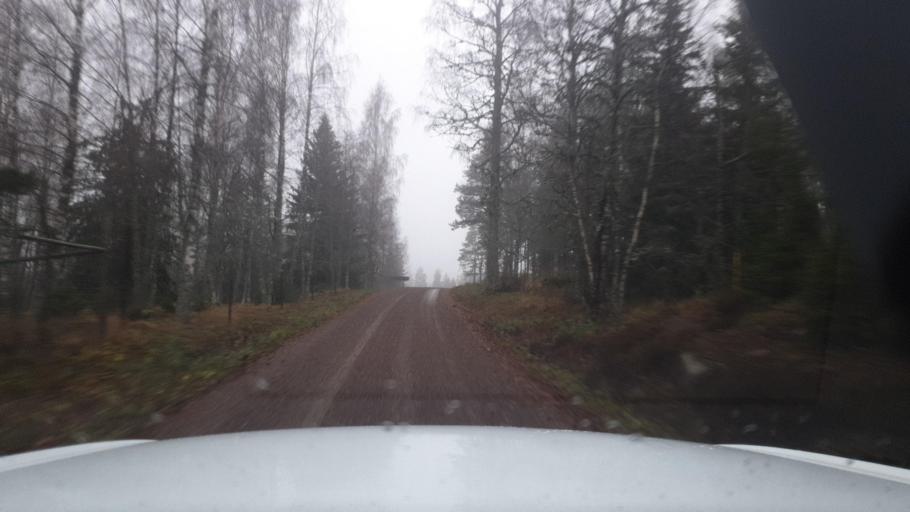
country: SE
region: Vaermland
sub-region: Torsby Kommun
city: Torsby
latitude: 59.9456
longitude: 12.7963
